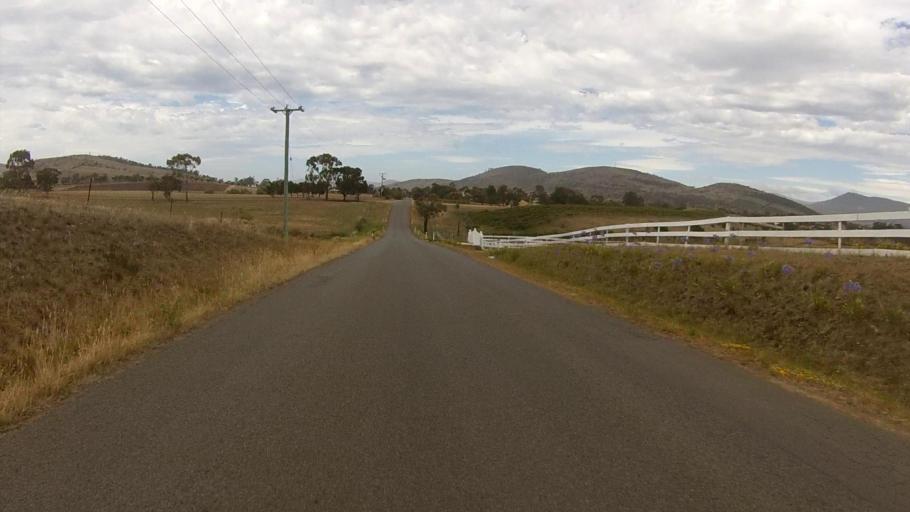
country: AU
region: Tasmania
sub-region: Clarence
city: Cambridge
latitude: -42.7272
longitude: 147.4494
